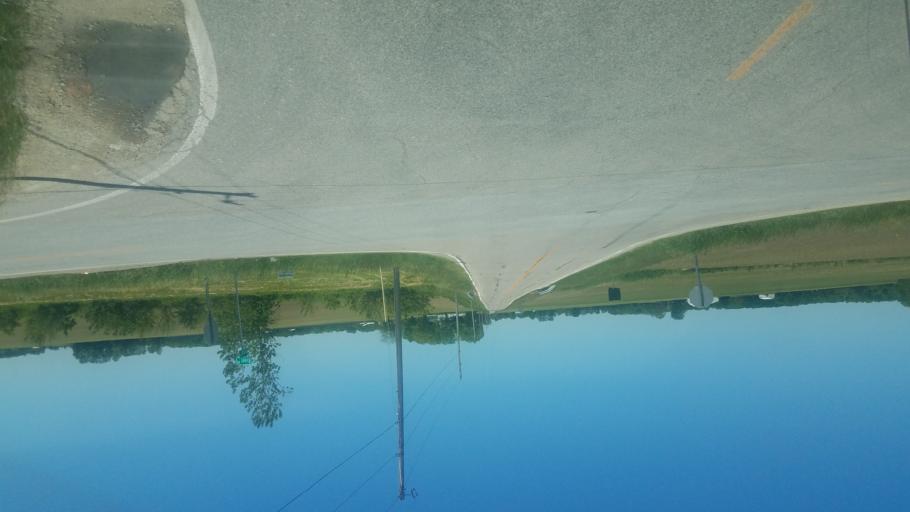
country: US
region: Ohio
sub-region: Shelby County
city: Sidney
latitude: 40.2157
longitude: -84.1915
